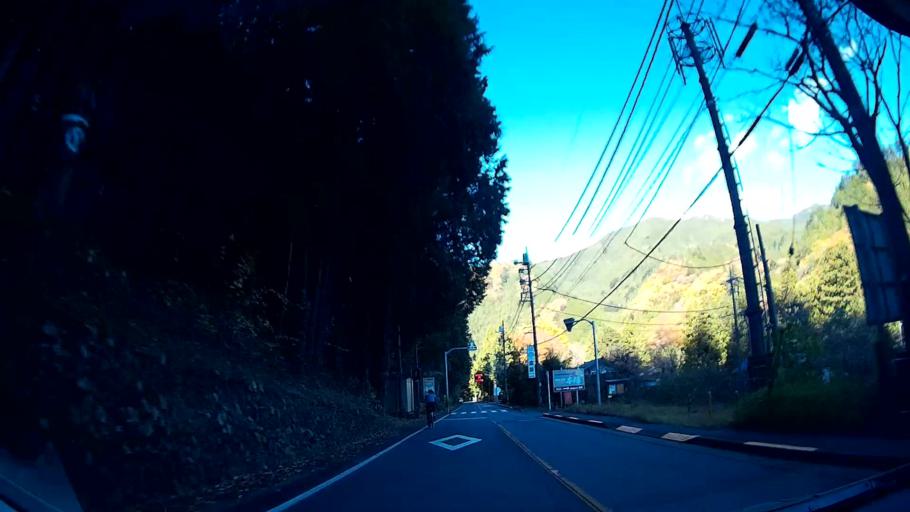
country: JP
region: Tokyo
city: Itsukaichi
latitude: 35.7233
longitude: 139.1733
